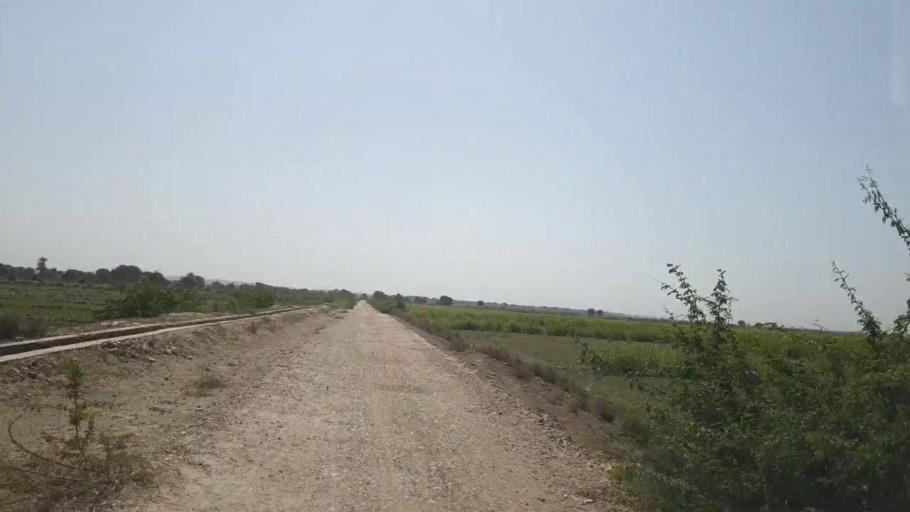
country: PK
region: Sindh
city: Naukot
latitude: 24.9032
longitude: 69.4875
